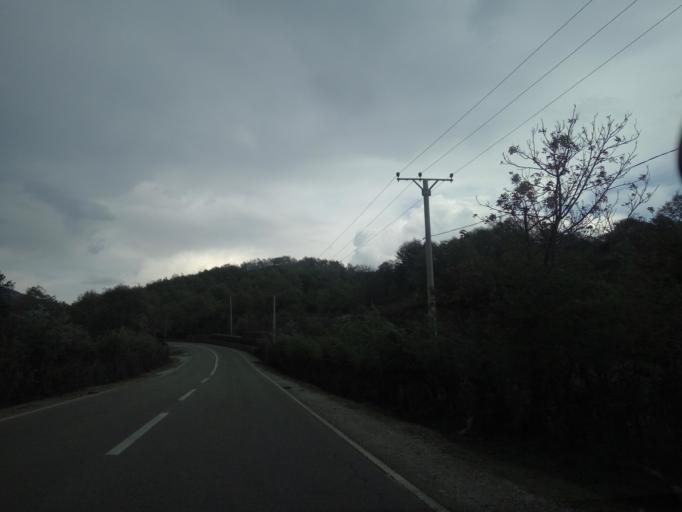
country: AL
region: Kukes
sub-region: Rrethi i Tropojes
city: Bytyc
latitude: 42.3896
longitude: 20.1782
